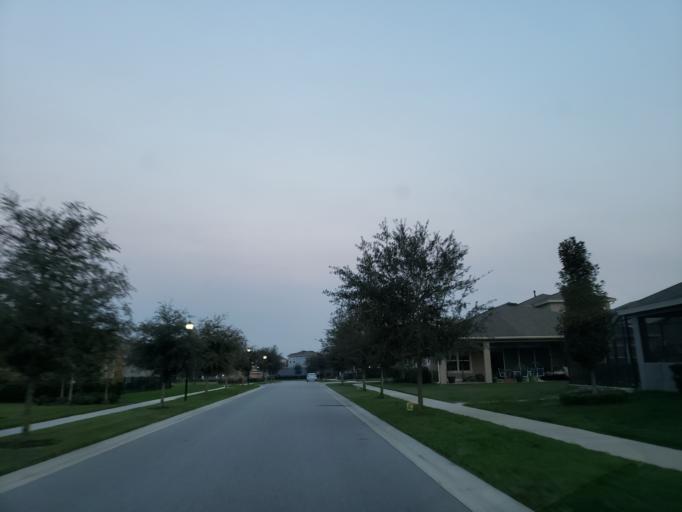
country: US
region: Florida
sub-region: Hillsborough County
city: Fish Hawk
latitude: 27.8497
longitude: -82.2508
